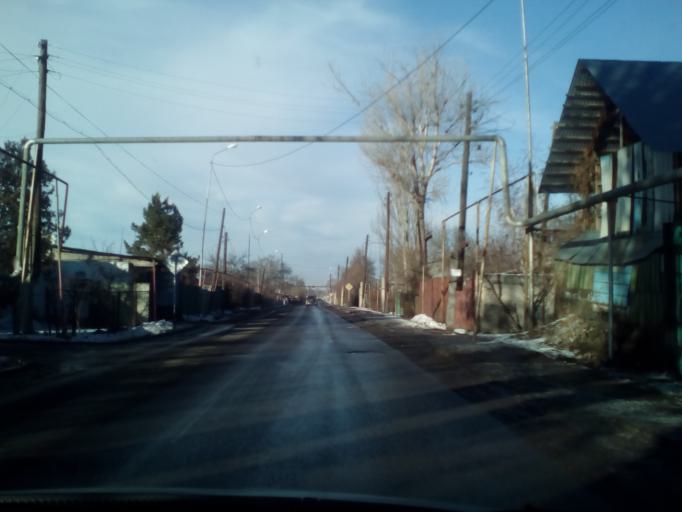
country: KZ
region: Almaty Oblysy
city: Burunday
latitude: 43.1661
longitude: 76.4169
